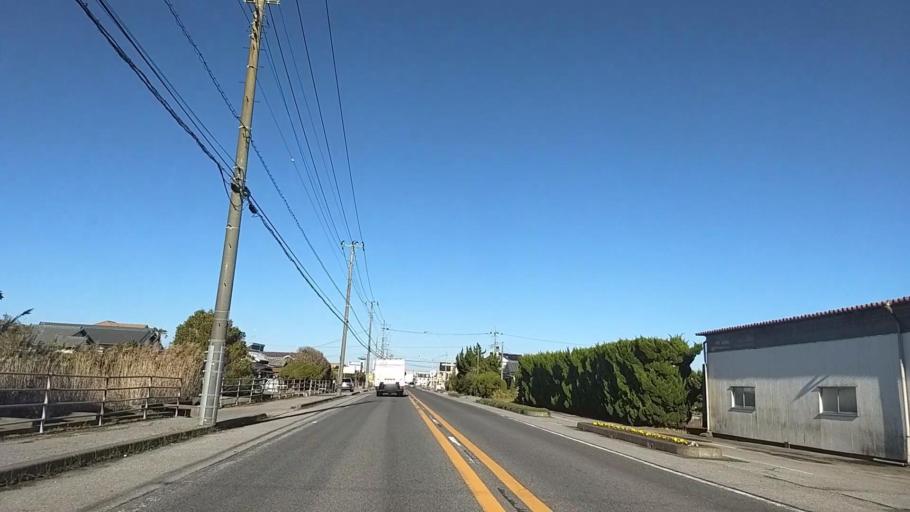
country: JP
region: Chiba
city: Togane
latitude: 35.5152
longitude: 140.4392
